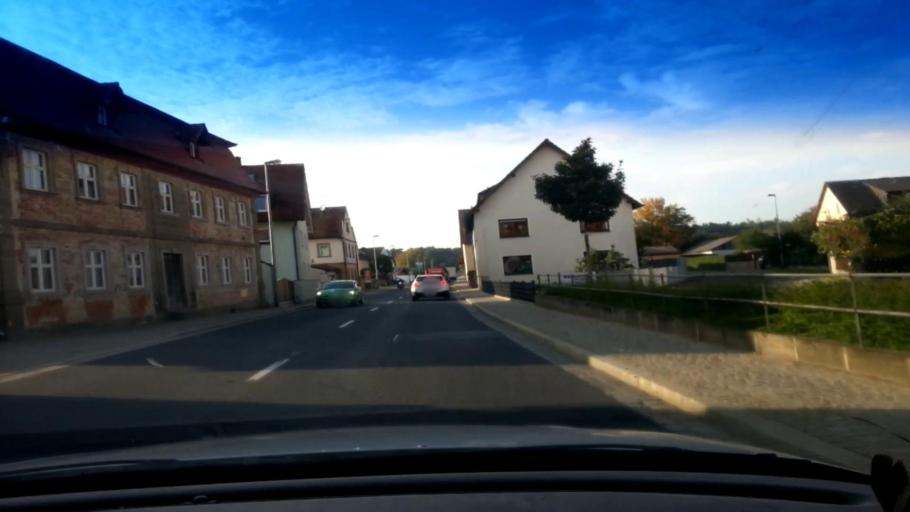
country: DE
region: Bavaria
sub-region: Upper Franconia
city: Strullendorf
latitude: 49.8456
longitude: 10.9675
